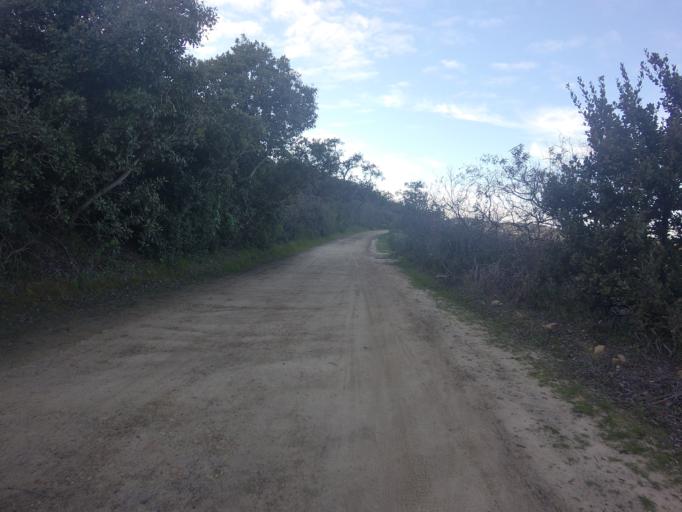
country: US
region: California
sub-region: Orange County
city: Laguna Beach
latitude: 33.5915
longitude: -117.7731
